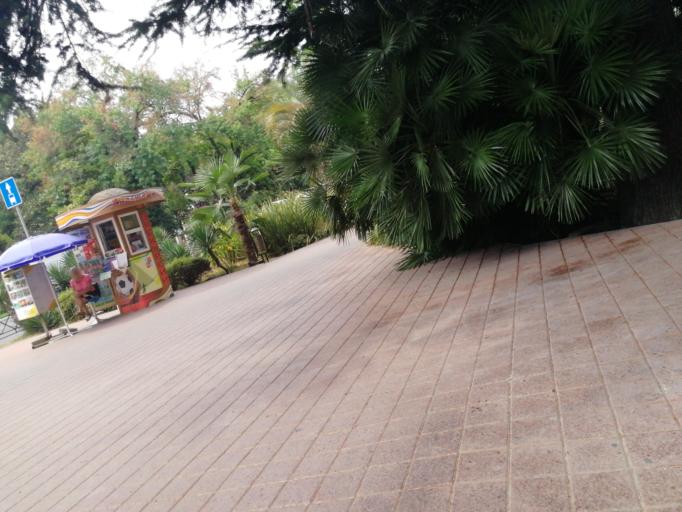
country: RU
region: Krasnodarskiy
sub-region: Sochi City
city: Sochi
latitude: 43.5827
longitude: 39.7220
